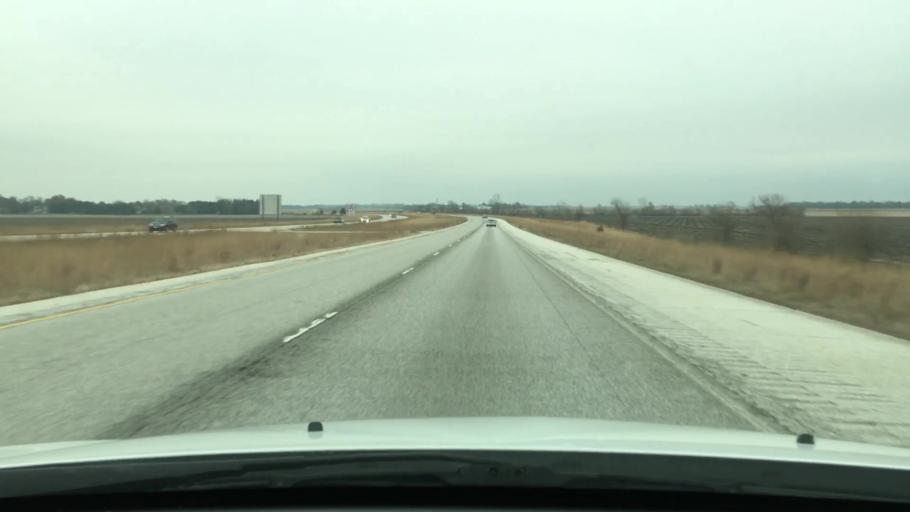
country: US
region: Illinois
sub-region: Morgan County
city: South Jacksonville
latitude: 39.6864
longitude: -90.2156
